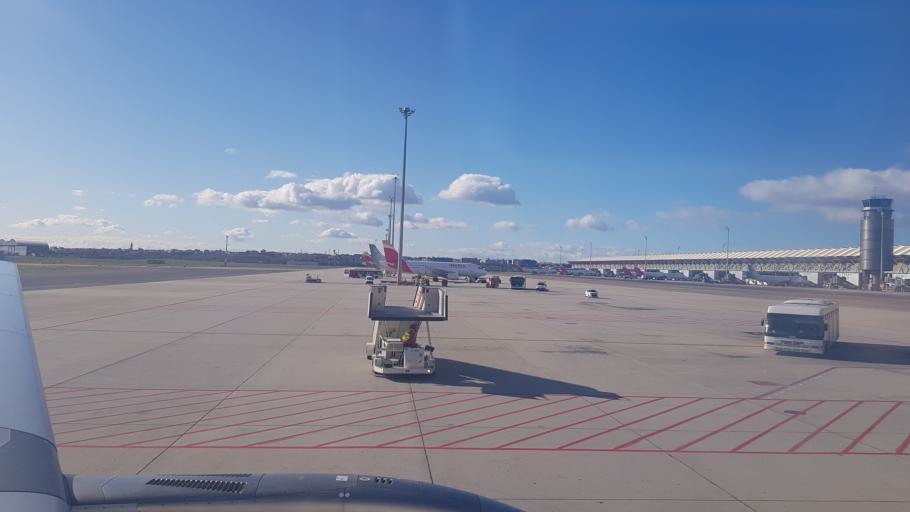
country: ES
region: Madrid
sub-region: Provincia de Madrid
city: Barajas de Madrid
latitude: 40.4948
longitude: -3.5863
